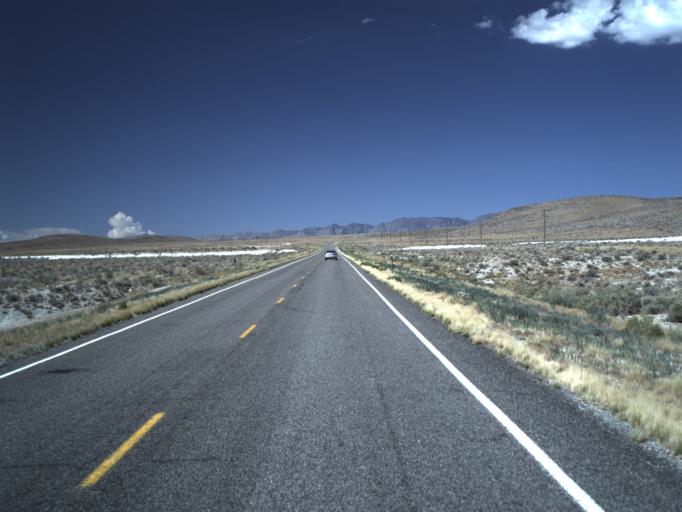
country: US
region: Utah
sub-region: Beaver County
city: Milford
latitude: 39.0624
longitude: -113.2414
